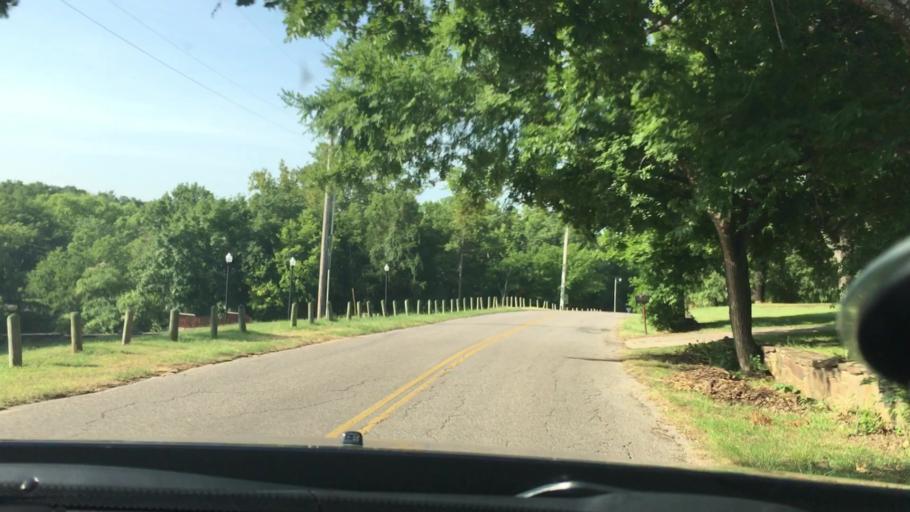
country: US
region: Oklahoma
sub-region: Pontotoc County
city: Ada
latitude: 34.7590
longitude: -96.6554
